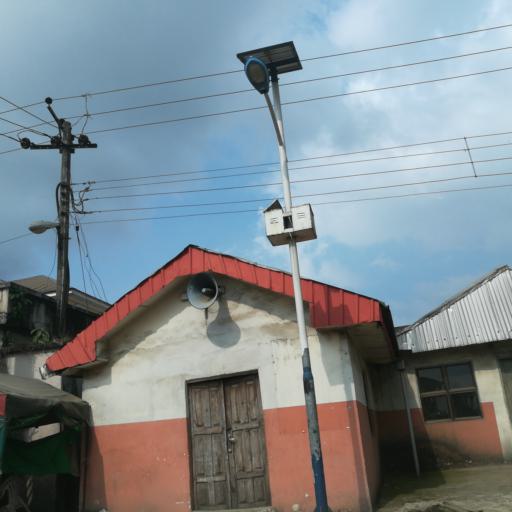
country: NG
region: Rivers
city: Okrika
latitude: 4.7895
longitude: 7.1190
